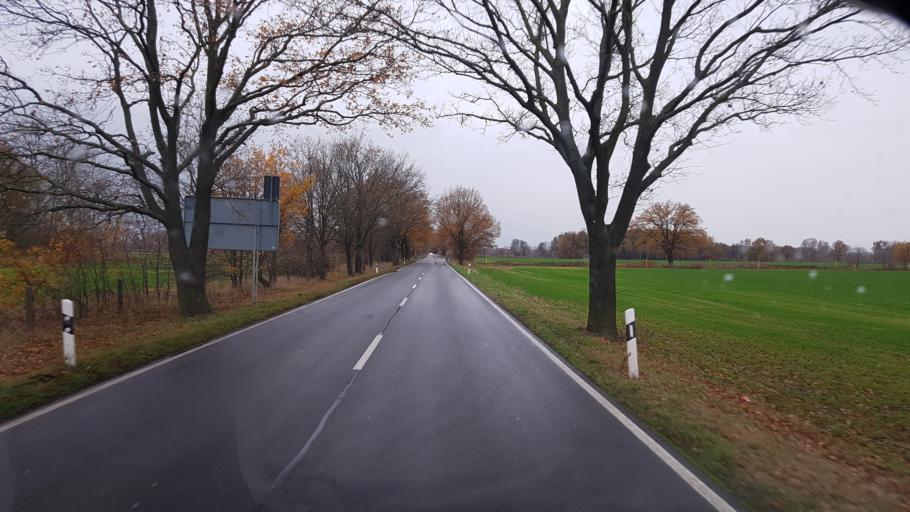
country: DE
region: Brandenburg
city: Schraden
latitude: 51.4649
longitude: 13.7125
